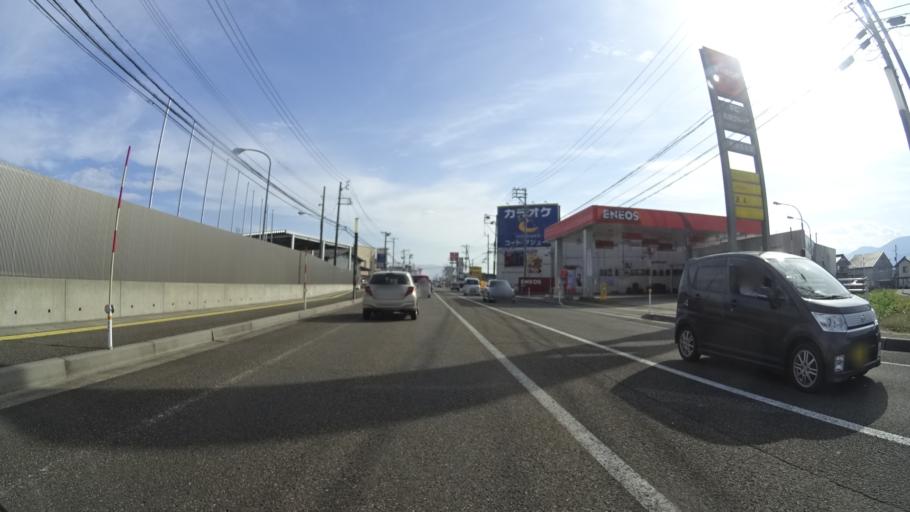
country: JP
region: Niigata
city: Joetsu
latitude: 37.1306
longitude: 138.2456
